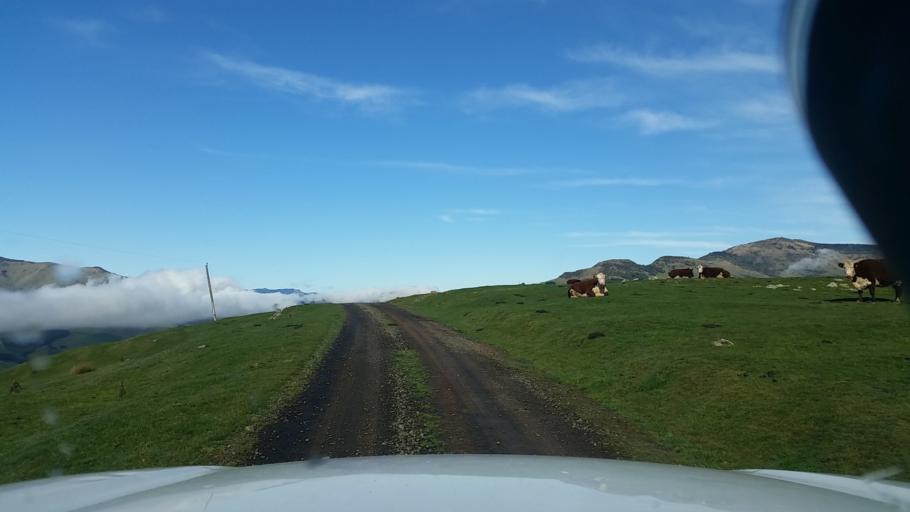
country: NZ
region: Canterbury
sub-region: Christchurch City
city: Christchurch
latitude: -43.6651
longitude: 172.8753
